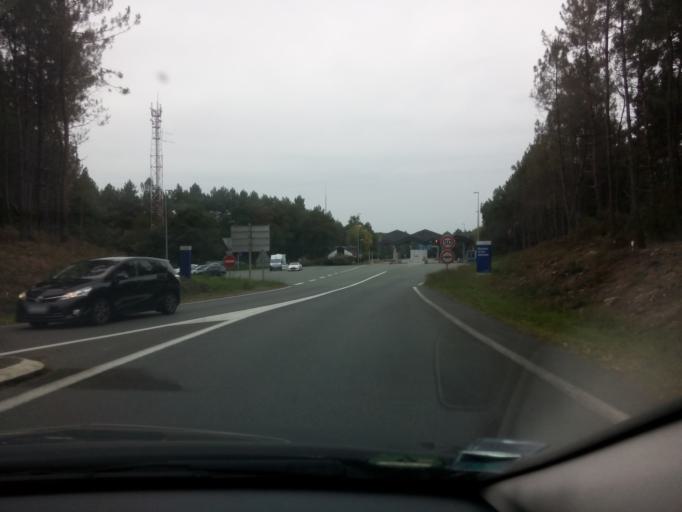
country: FR
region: Pays de la Loire
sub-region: Departement de Maine-et-Loire
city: Seiches-sur-le-Loir
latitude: 47.5679
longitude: -0.3276
